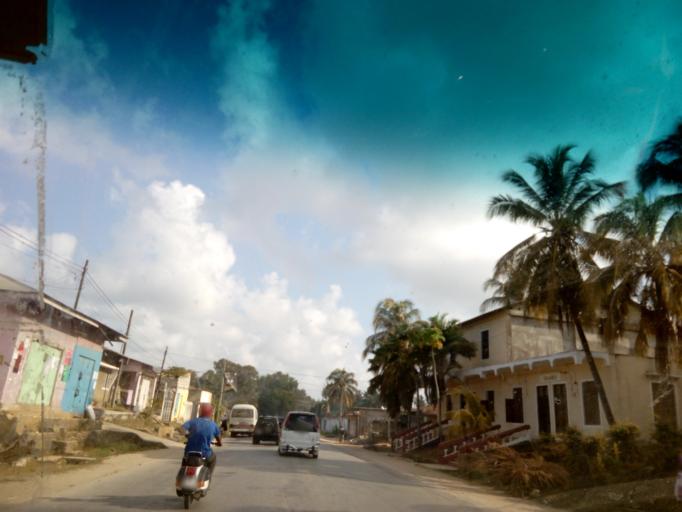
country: TZ
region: Zanzibar Urban/West
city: Zanzibar
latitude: -6.0960
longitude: 39.2191
